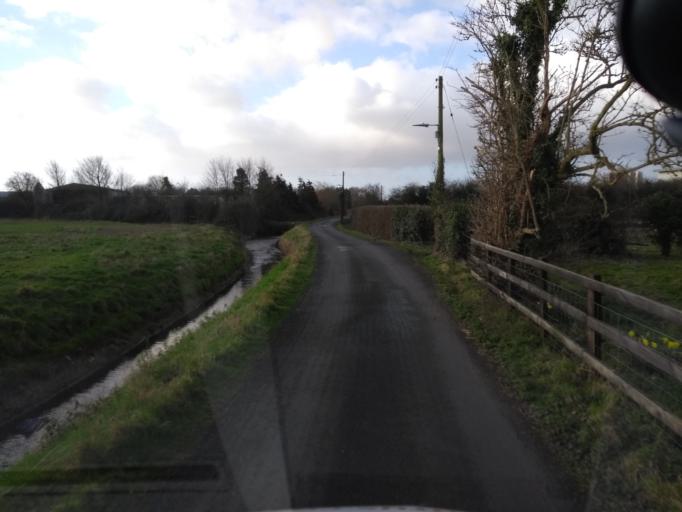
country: GB
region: England
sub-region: Somerset
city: Highbridge
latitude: 51.2247
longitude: -2.9606
